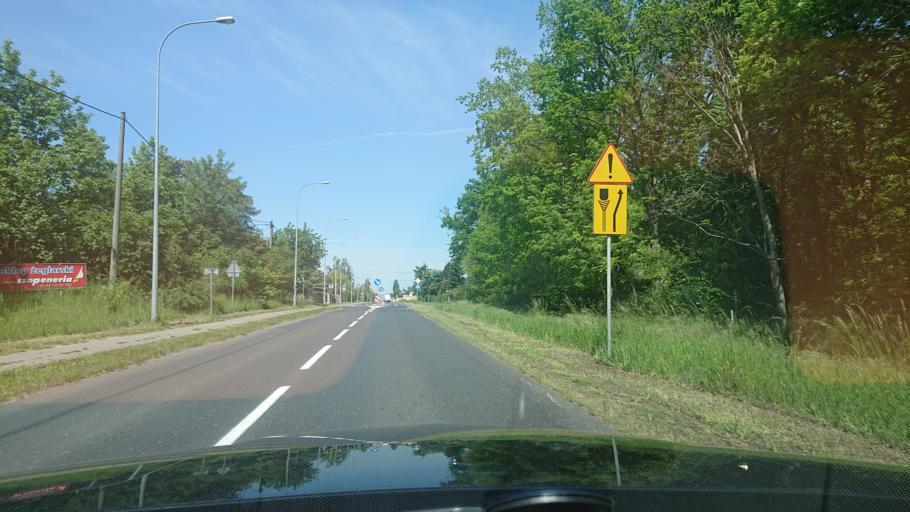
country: PL
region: Greater Poland Voivodeship
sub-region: Powiat gnieznienski
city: Gniezno
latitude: 52.5075
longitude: 17.6217
